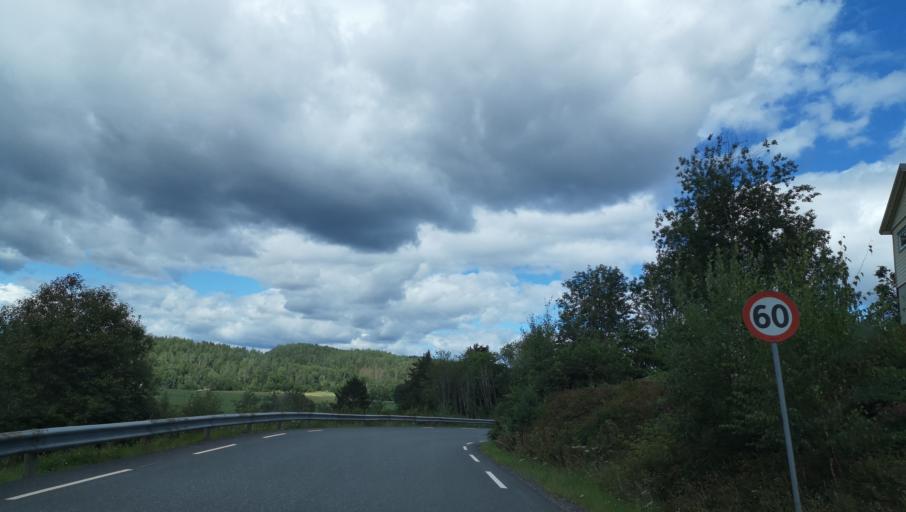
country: NO
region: Ostfold
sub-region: Hobol
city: Tomter
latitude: 59.6687
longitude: 11.0044
